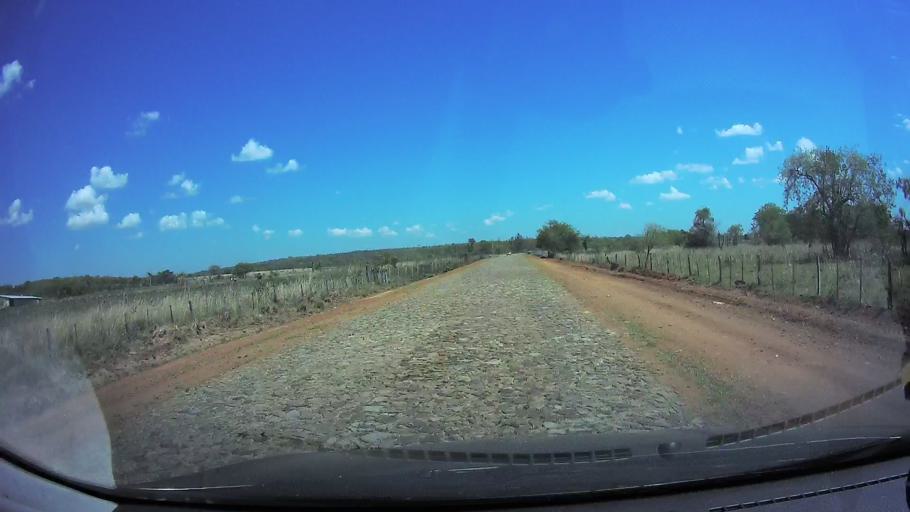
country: PY
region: Cordillera
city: Emboscada
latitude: -25.1243
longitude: -57.2733
